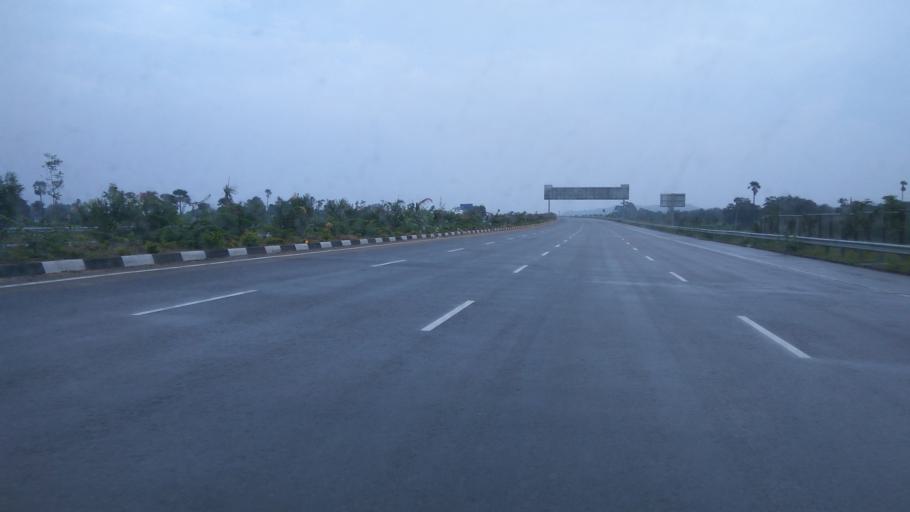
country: IN
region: Telangana
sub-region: Rangareddi
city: Ghatkesar
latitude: 17.4595
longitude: 78.6700
